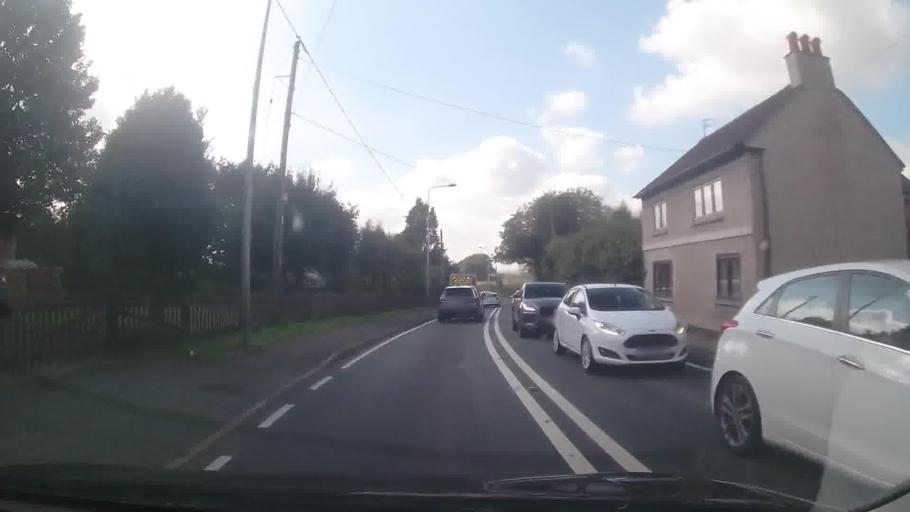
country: GB
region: England
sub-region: Cheshire West and Chester
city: Weaverham
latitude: 53.2883
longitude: -2.5935
